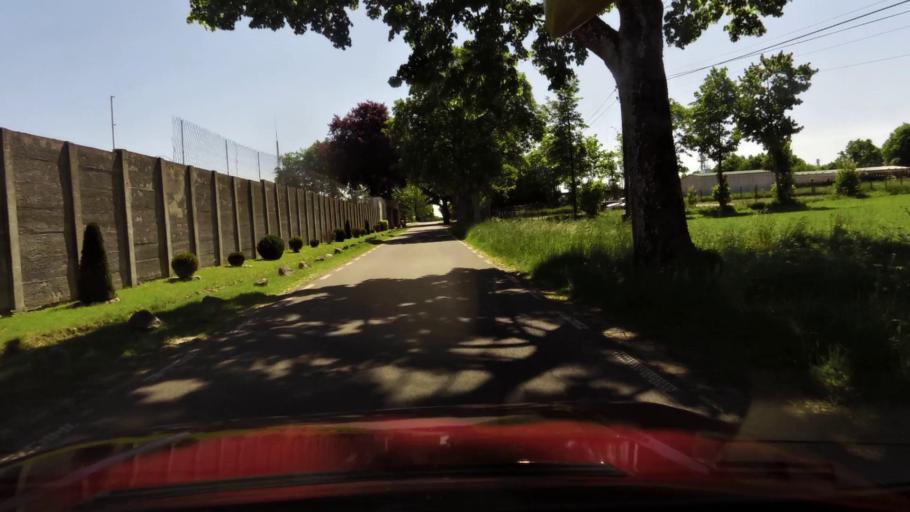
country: PL
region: West Pomeranian Voivodeship
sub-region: Powiat koszalinski
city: Bobolice
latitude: 54.0045
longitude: 16.6724
